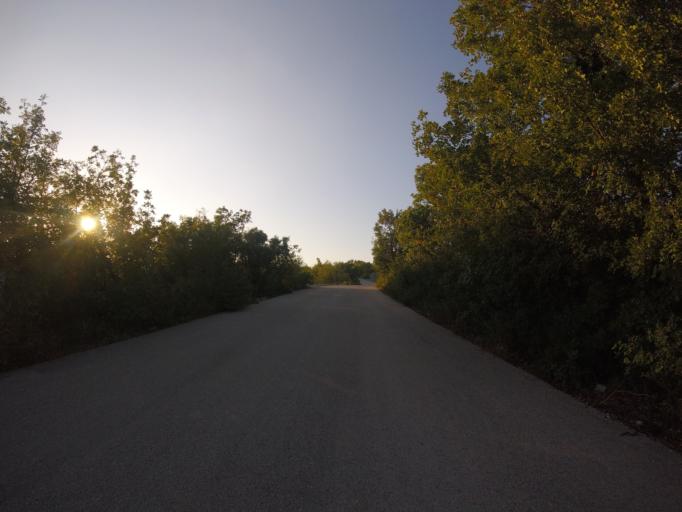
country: HR
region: Primorsko-Goranska
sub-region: Grad Crikvenica
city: Jadranovo
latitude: 45.2073
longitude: 14.6452
